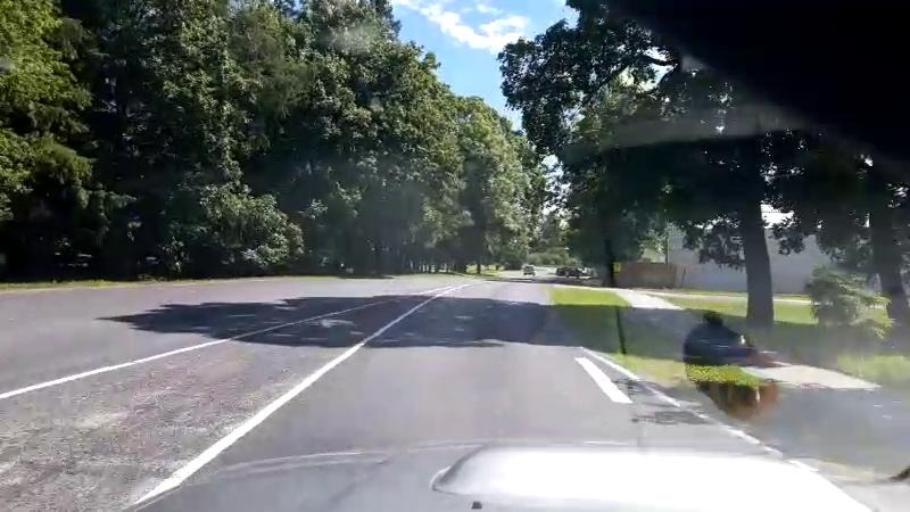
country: EE
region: Jaervamaa
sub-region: Jaerva-Jaani vald
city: Jarva-Jaani
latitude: 59.0462
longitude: 25.8821
